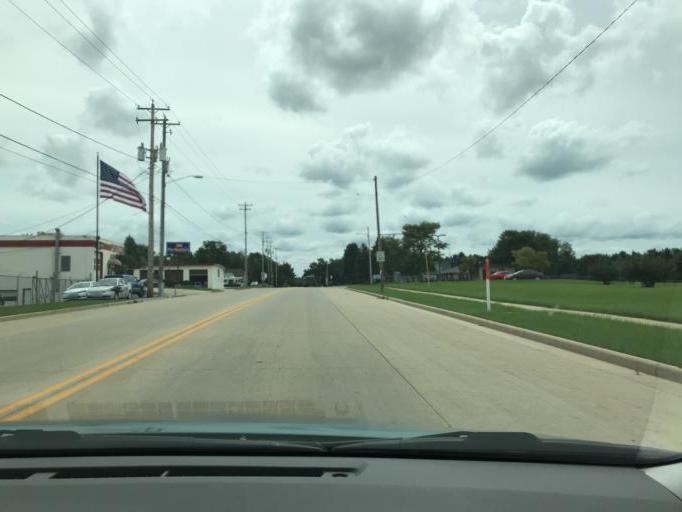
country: US
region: Wisconsin
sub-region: Racine County
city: Burlington
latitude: 42.6661
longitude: -88.2652
